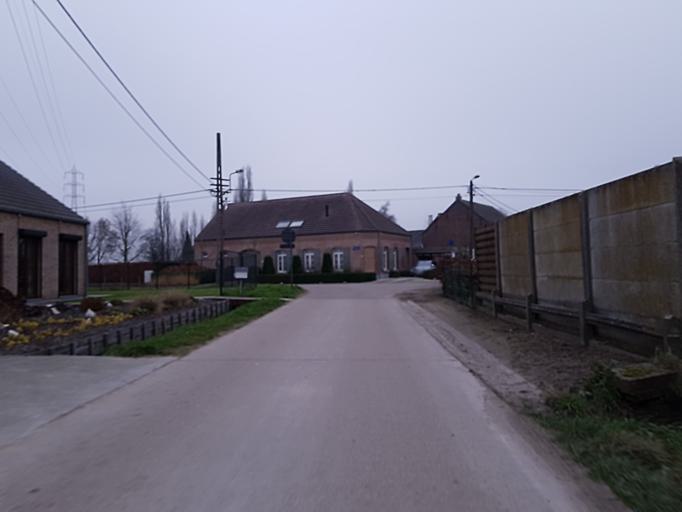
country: BE
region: Flanders
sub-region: Provincie Vlaams-Brabant
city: Kapelle-op-den-Bos
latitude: 51.0267
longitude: 4.4109
